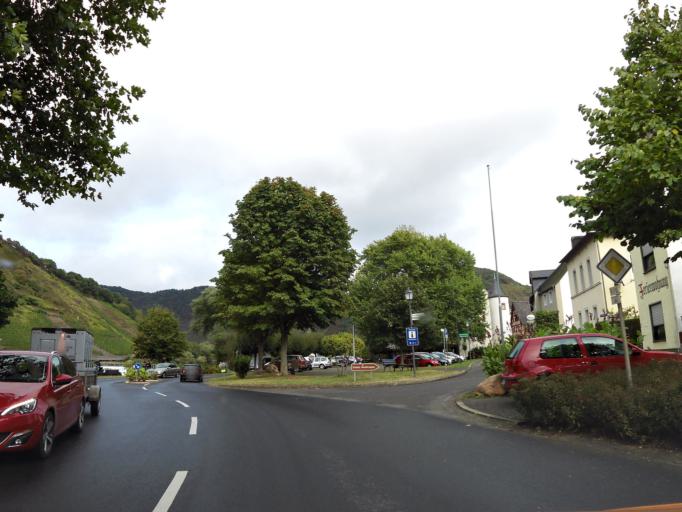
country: DE
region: Rheinland-Pfalz
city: Bruttig-Fankel
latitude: 50.1334
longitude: 7.2316
